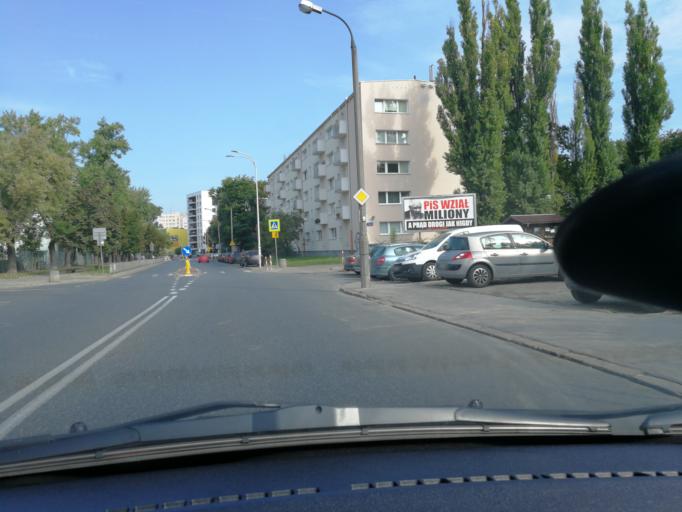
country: PL
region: Masovian Voivodeship
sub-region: Warszawa
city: Bemowo
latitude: 52.2329
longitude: 20.9414
